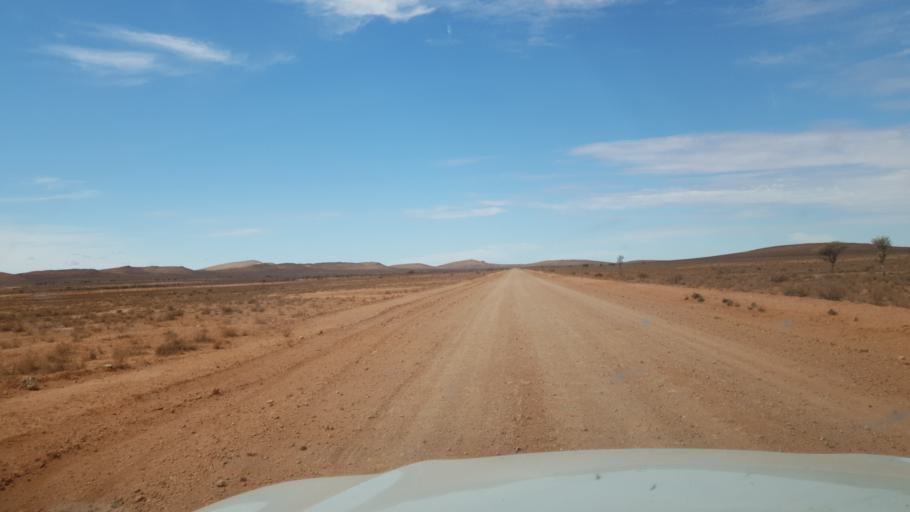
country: AU
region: South Australia
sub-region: Peterborough
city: Peterborough
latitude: -32.2279
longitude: 139.3926
